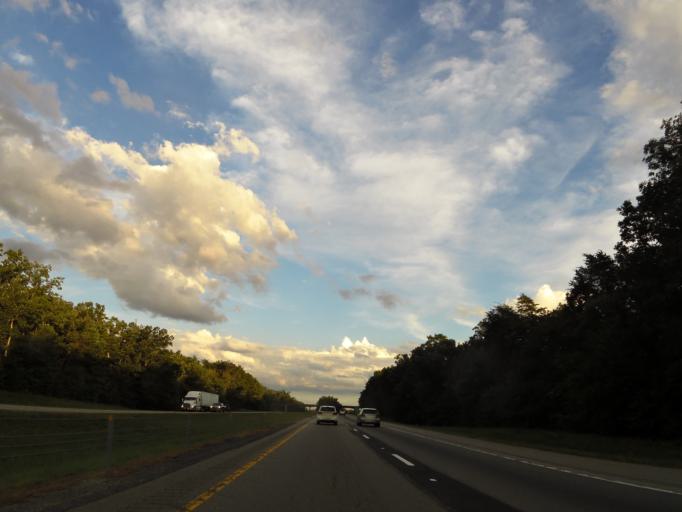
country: US
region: Tennessee
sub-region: Putnam County
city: Monterey
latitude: 36.0675
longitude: -85.1899
